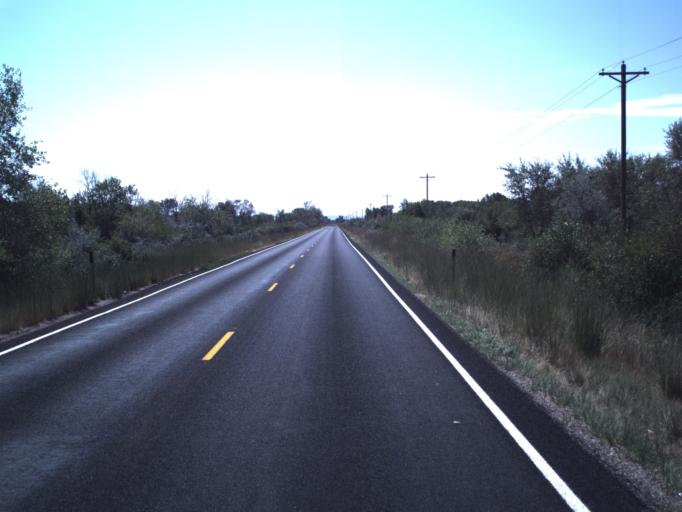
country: US
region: Utah
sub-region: Duchesne County
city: Roosevelt
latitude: 40.4243
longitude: -109.9239
